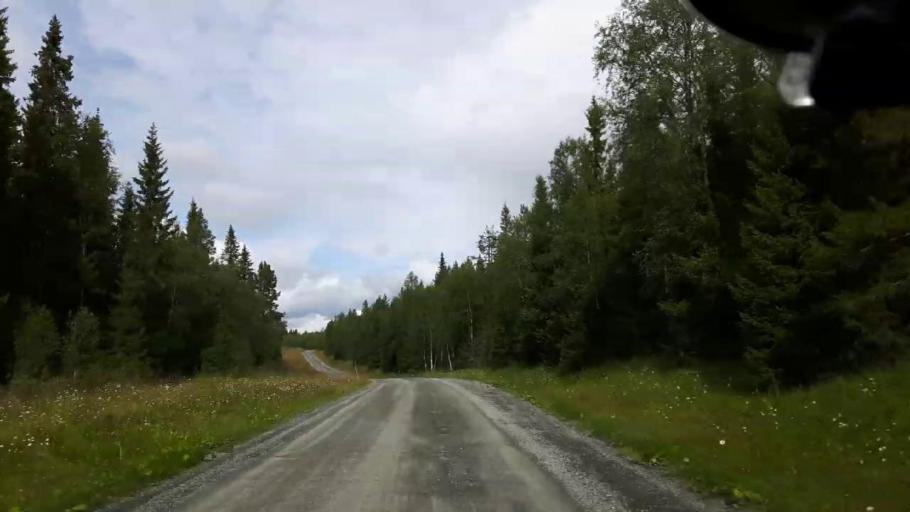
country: SE
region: Jaemtland
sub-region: Krokoms Kommun
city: Valla
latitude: 63.5487
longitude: 13.9165
